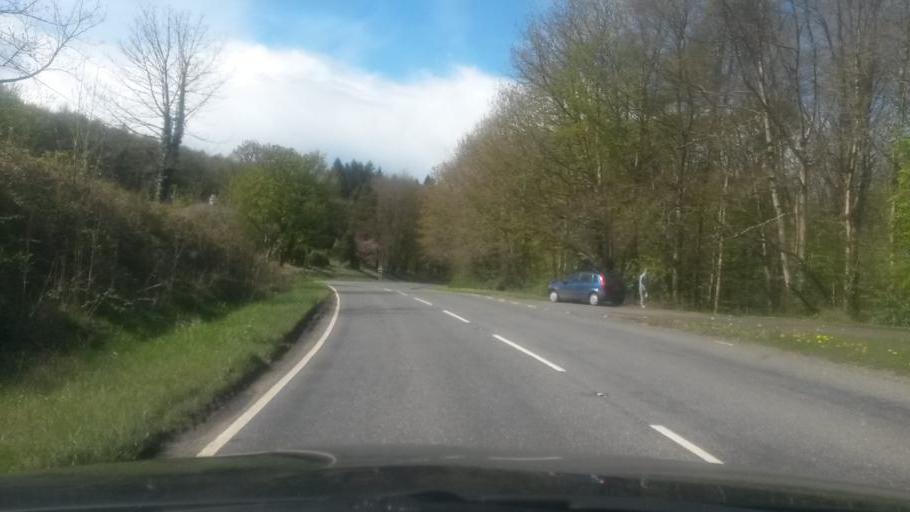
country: GB
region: Northern Ireland
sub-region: Fermanagh District
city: Enniskillen
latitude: 54.4105
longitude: -7.7233
